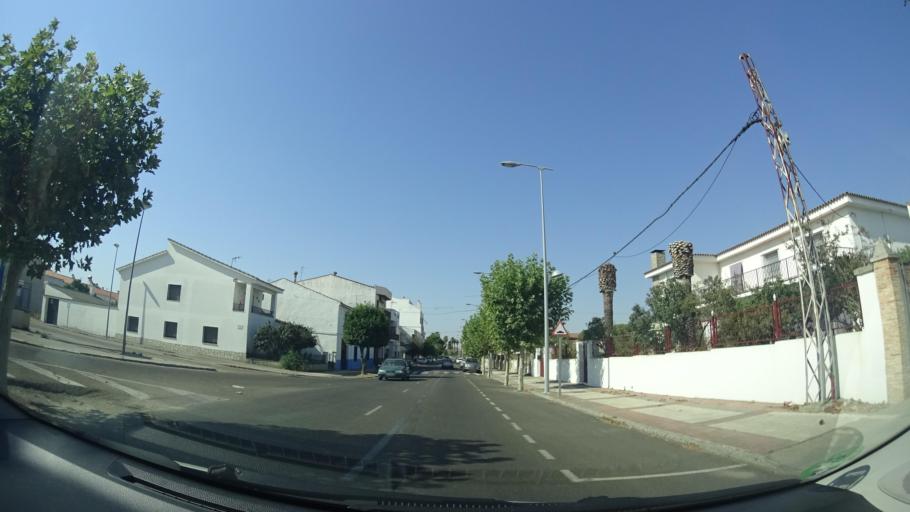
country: ES
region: Extremadura
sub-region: Provincia de Caceres
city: Miajadas
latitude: 39.1574
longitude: -5.9000
